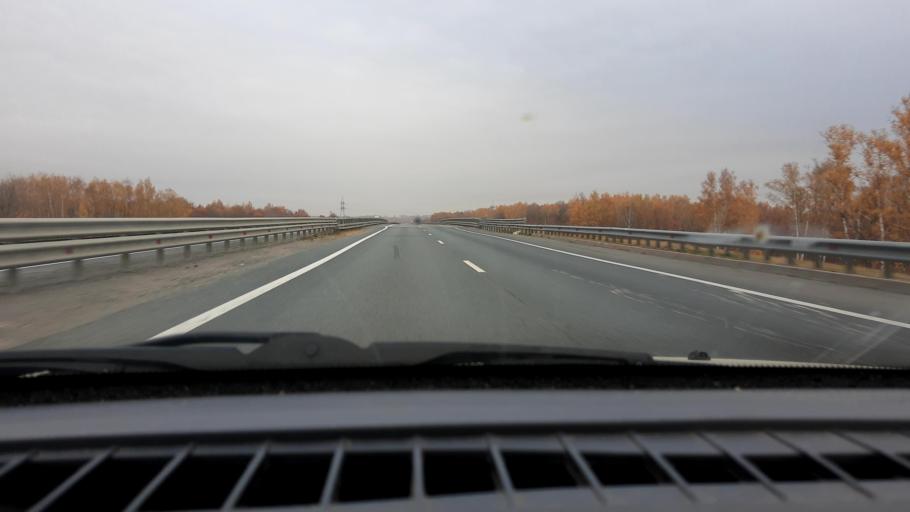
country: RU
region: Nizjnij Novgorod
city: Burevestnik
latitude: 56.1317
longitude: 43.7780
